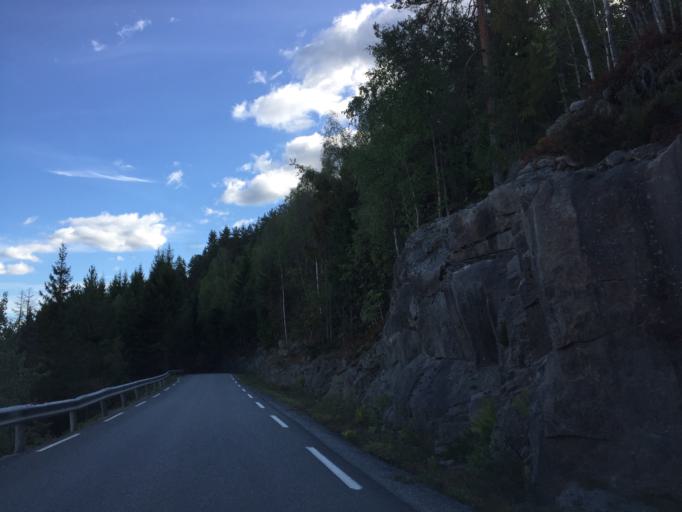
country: NO
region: Buskerud
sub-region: Ovre Eiker
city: Hokksund
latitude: 59.6527
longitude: 9.9149
